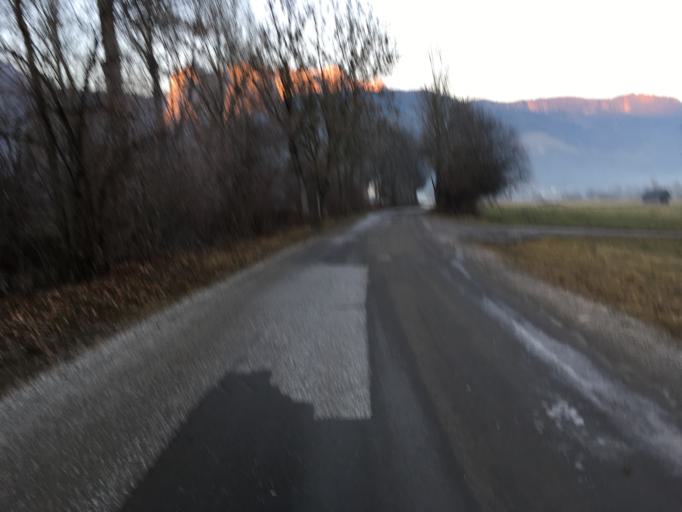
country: AT
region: Styria
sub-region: Politischer Bezirk Liezen
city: Weissenbach bei Liezen
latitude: 47.5591
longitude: 14.2068
